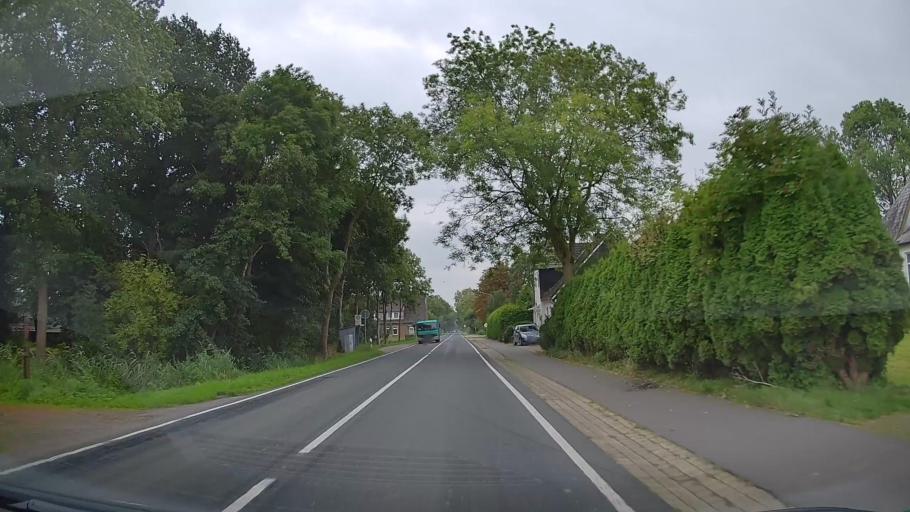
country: DE
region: Lower Saxony
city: Freiburg
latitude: 53.8125
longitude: 9.3033
